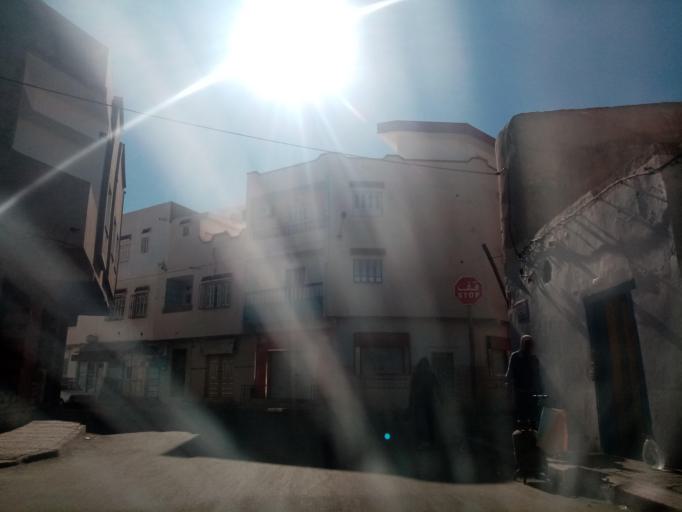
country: TN
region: Qabis
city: Gabes
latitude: 33.8788
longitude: 10.0900
